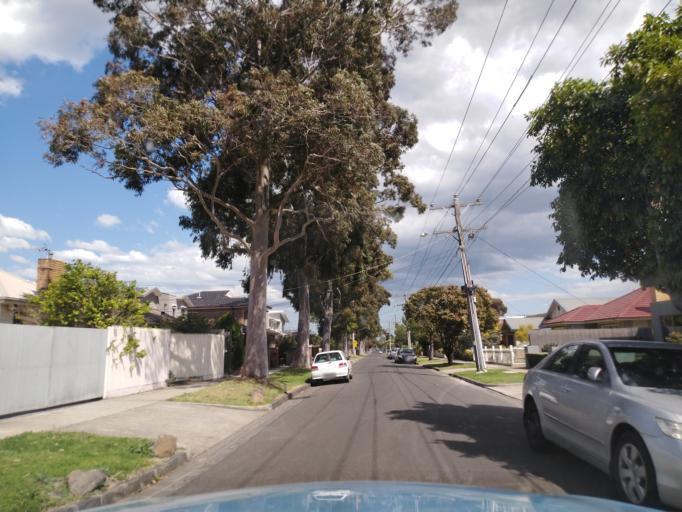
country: AU
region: Victoria
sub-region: Hobsons Bay
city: South Kingsville
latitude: -37.8338
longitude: 144.8687
